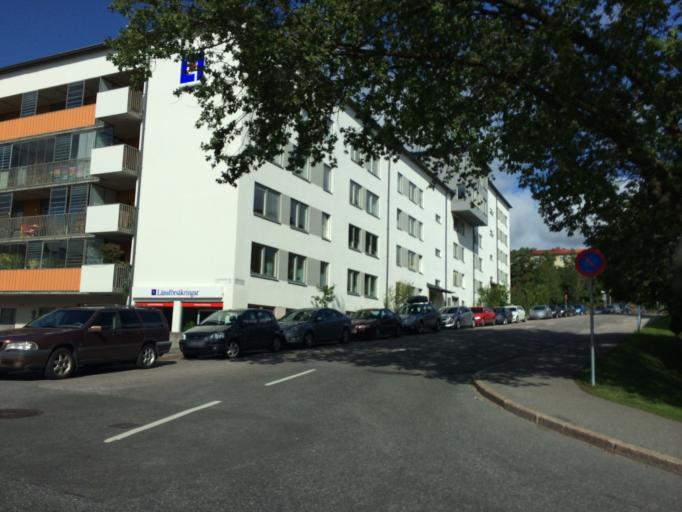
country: SE
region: Stockholm
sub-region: Stockholms Kommun
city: Arsta
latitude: 59.3002
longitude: 17.9954
